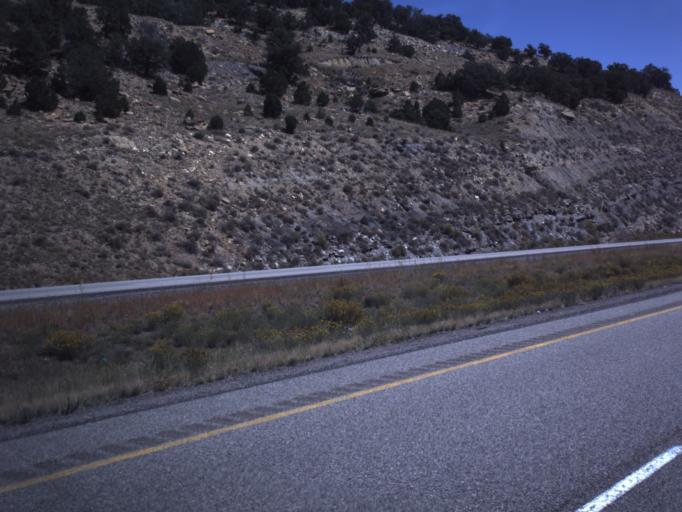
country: US
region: Utah
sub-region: Wayne County
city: Loa
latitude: 38.7608
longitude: -111.4562
